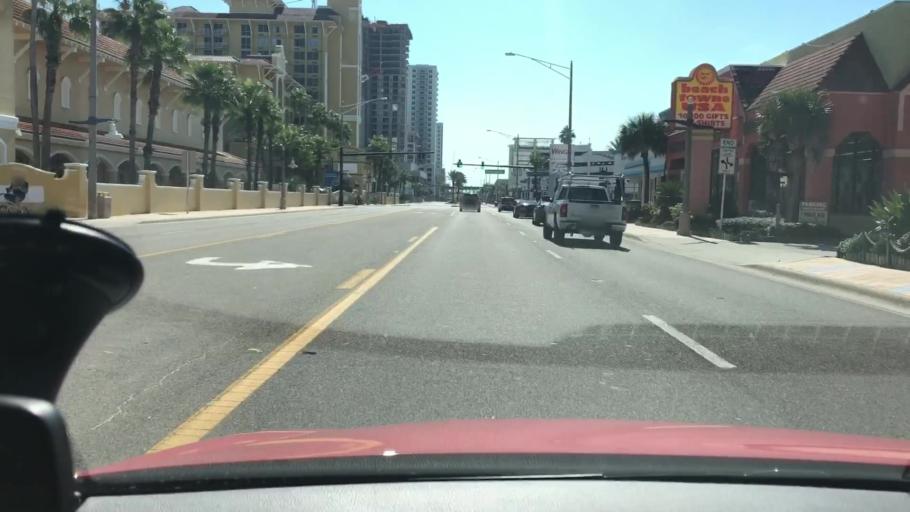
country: US
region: Florida
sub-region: Volusia County
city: Holly Hill
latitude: 29.2364
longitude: -81.0129
